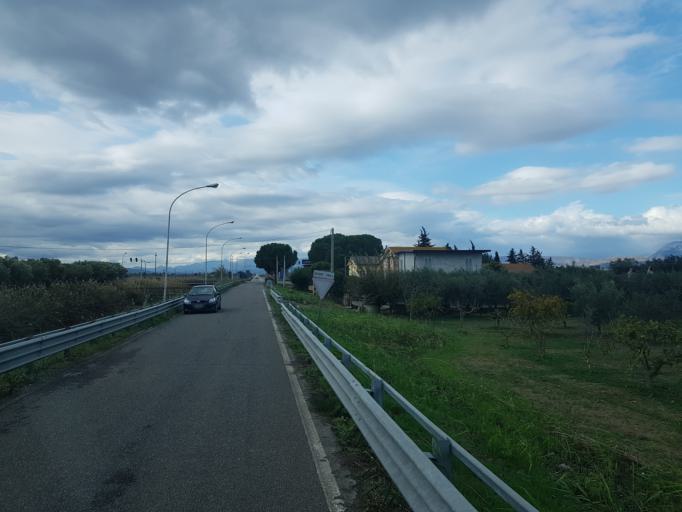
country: IT
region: Calabria
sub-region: Provincia di Cosenza
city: Sibari
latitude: 39.7267
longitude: 16.4858
